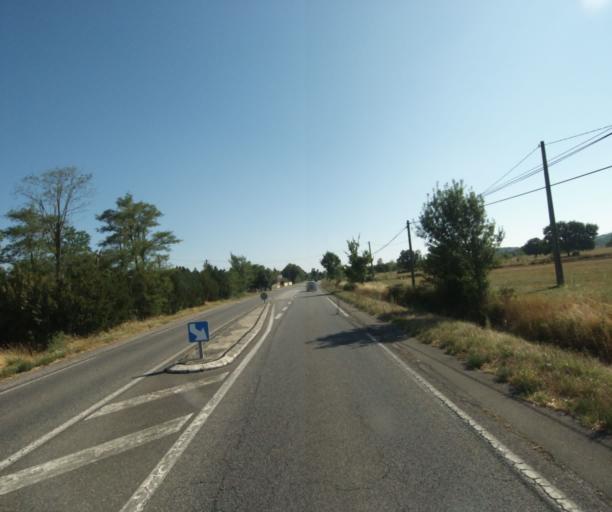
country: FR
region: Midi-Pyrenees
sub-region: Departement de la Haute-Garonne
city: Revel
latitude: 43.4819
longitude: 2.0227
